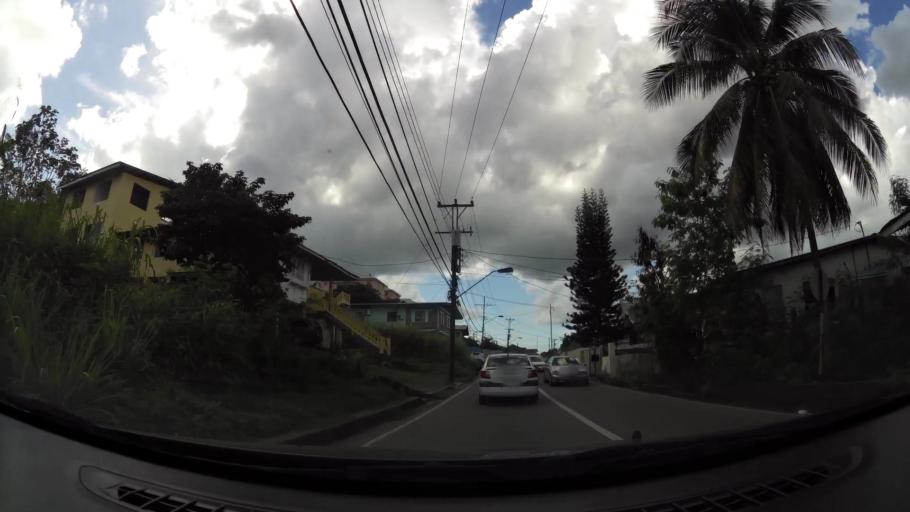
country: TT
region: City of San Fernando
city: Mon Repos
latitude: 10.2852
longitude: -61.4542
